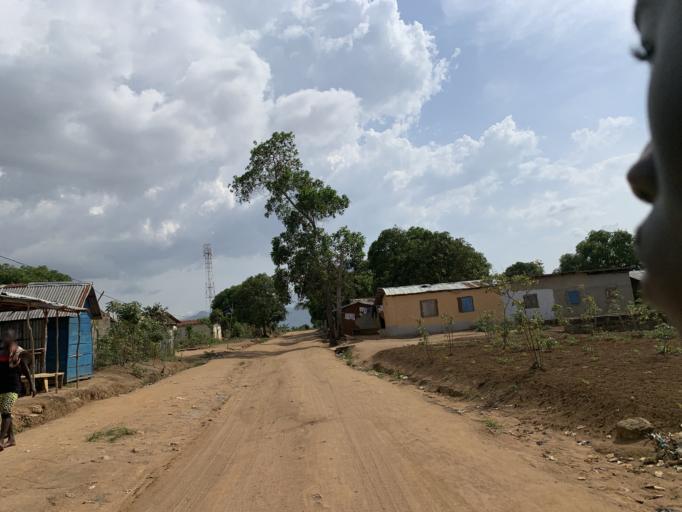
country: SL
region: Western Area
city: Waterloo
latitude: 8.3475
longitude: -13.0390
